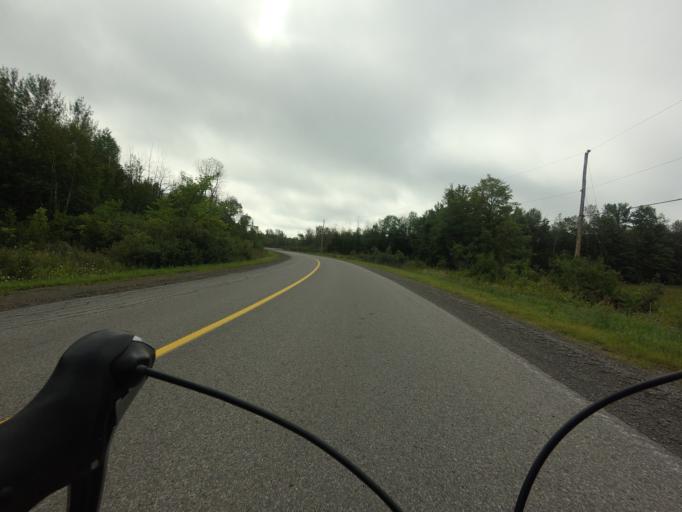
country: CA
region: Ontario
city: Bells Corners
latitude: 45.0693
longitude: -75.7310
